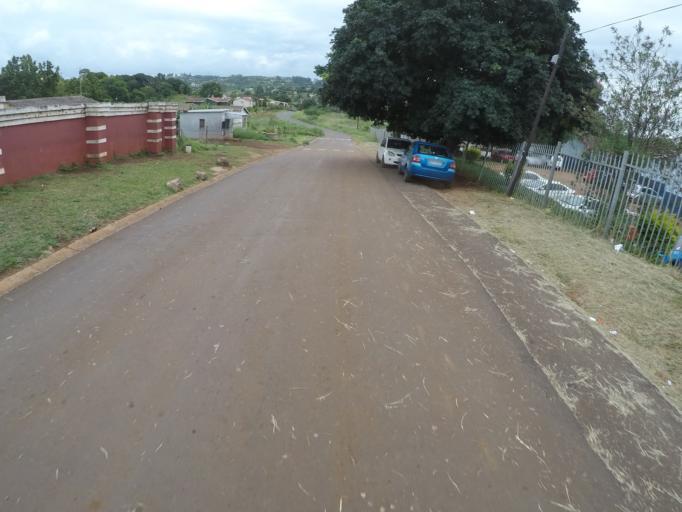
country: ZA
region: KwaZulu-Natal
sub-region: uThungulu District Municipality
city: Empangeni
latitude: -28.7694
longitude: 31.8666
